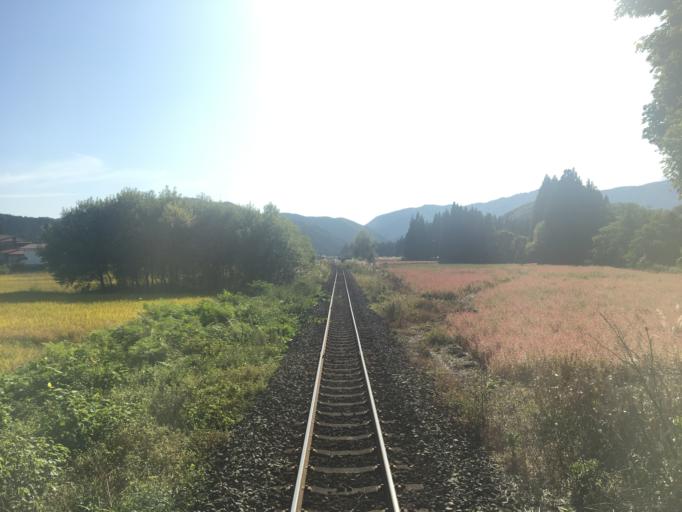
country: JP
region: Akita
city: Kakunodatemachi
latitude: 39.7458
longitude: 140.5924
